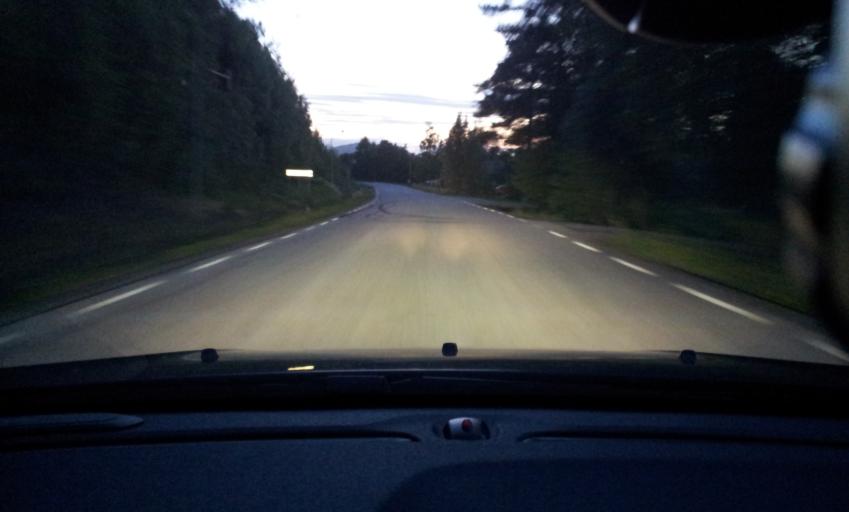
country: SE
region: Jaemtland
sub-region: Bergs Kommun
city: Hoverberg
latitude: 62.7795
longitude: 14.5141
